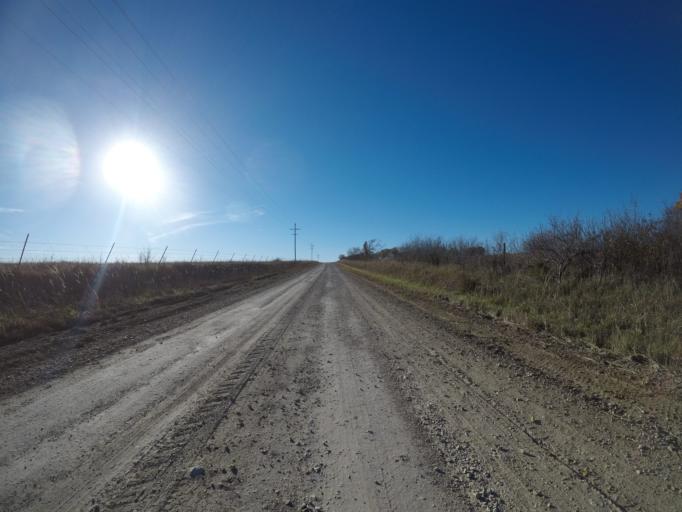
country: US
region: Kansas
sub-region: Riley County
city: Ogden
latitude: 39.2615
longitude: -96.7291
